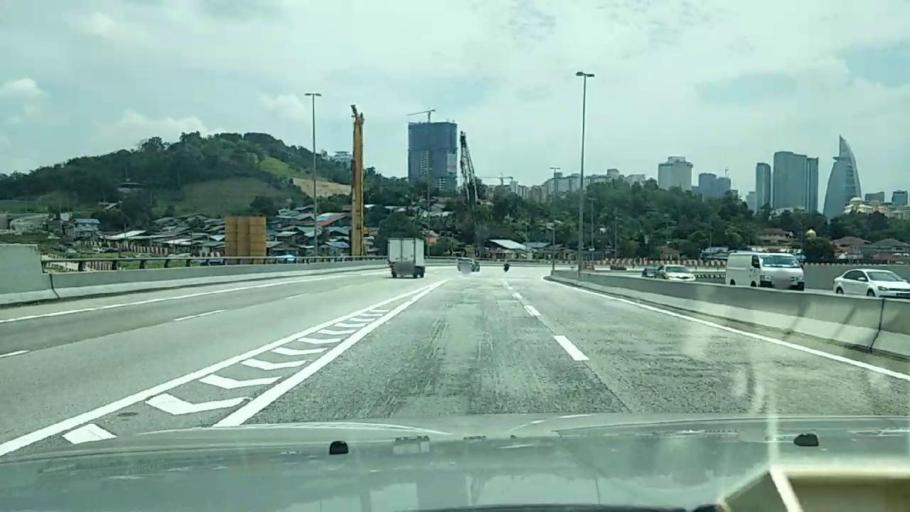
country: MY
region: Kuala Lumpur
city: Kuala Lumpur
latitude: 3.0944
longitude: 101.6699
